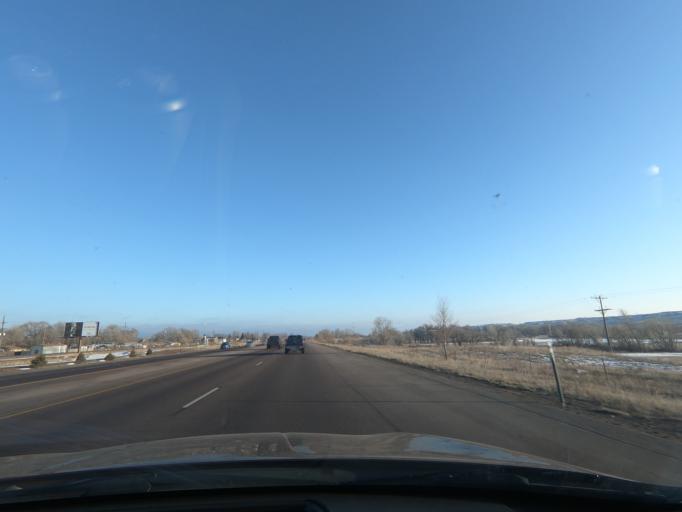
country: US
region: Colorado
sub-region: El Paso County
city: Stratmoor
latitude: 38.7644
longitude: -104.7570
